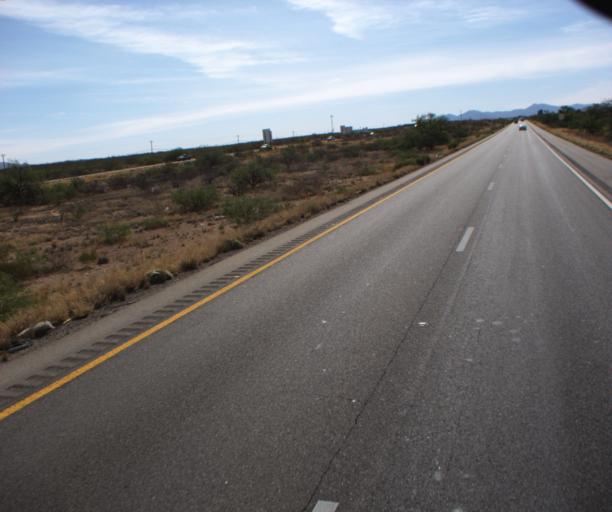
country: US
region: Arizona
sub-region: Pima County
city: Vail
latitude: 32.0215
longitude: -110.7124
